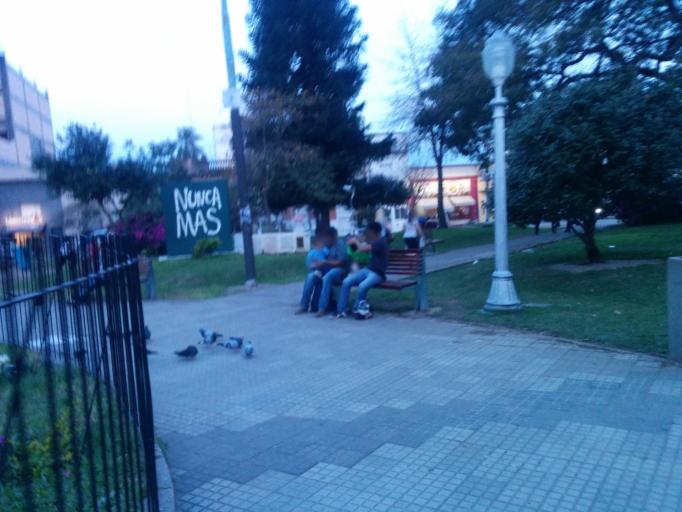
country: AR
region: Entre Rios
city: Concordia
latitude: -31.3920
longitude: -58.0171
